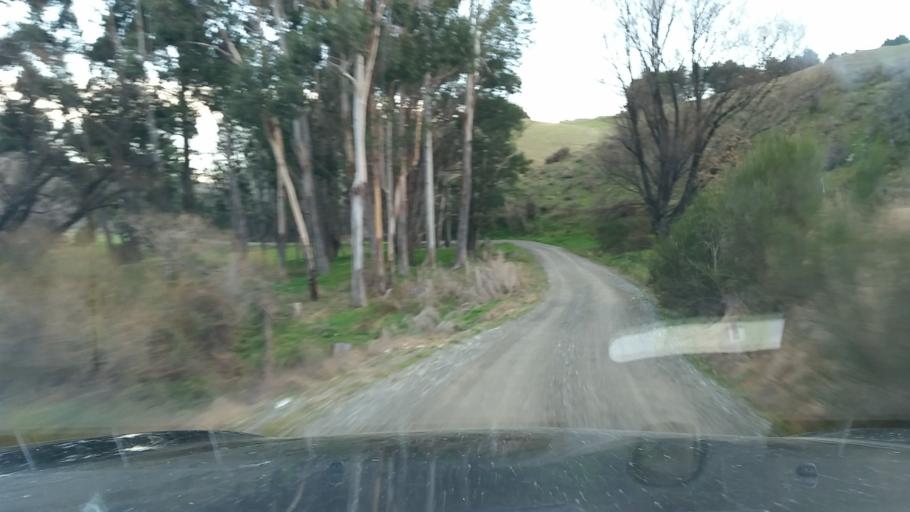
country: NZ
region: Marlborough
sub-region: Marlborough District
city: Blenheim
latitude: -41.4990
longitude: 173.5890
